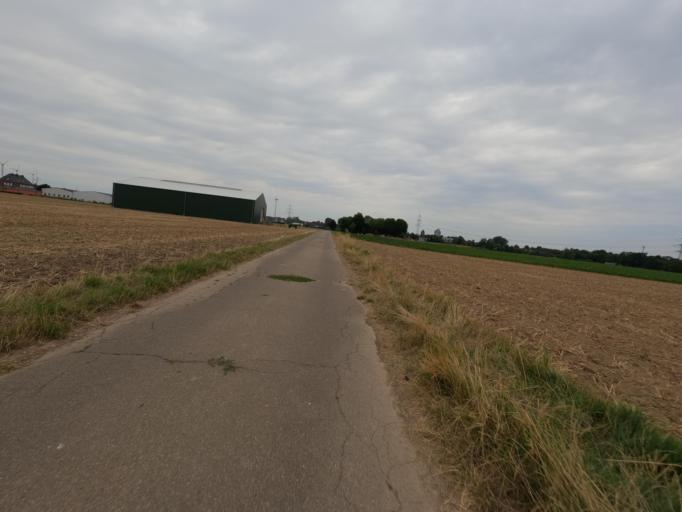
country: DE
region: North Rhine-Westphalia
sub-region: Regierungsbezirk Koln
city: Aldenhoven
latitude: 50.9312
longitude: 6.3004
